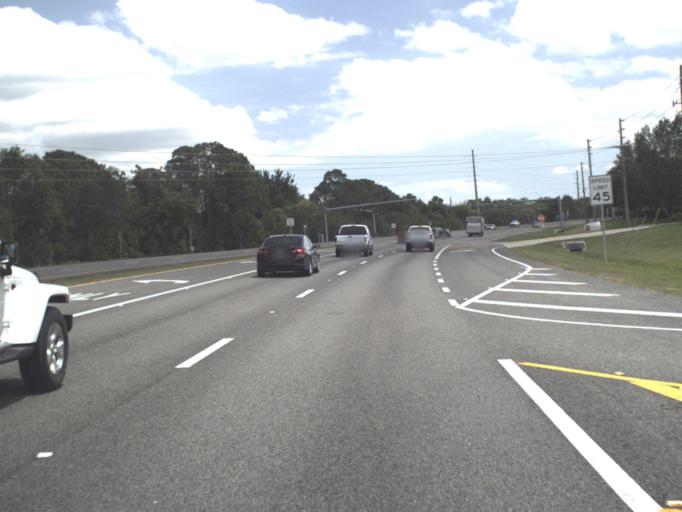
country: US
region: Florida
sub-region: Brevard County
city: Titusville
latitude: 28.5536
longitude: -80.8425
